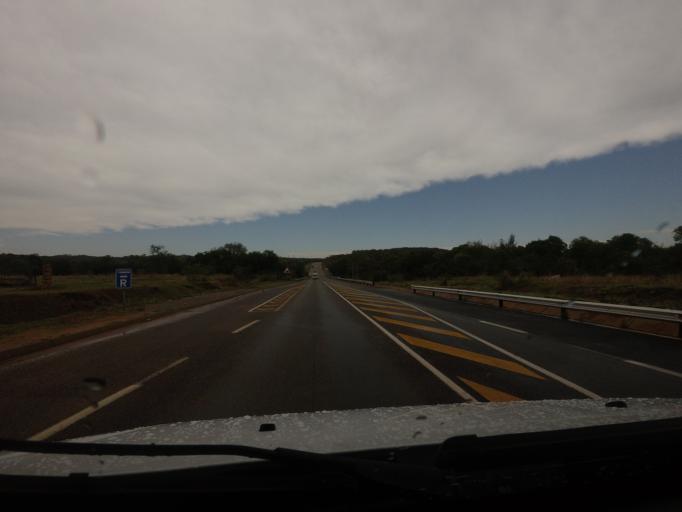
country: ZA
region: Gauteng
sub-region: City of Tshwane Metropolitan Municipality
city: Cullinan
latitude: -25.6075
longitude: 28.3681
